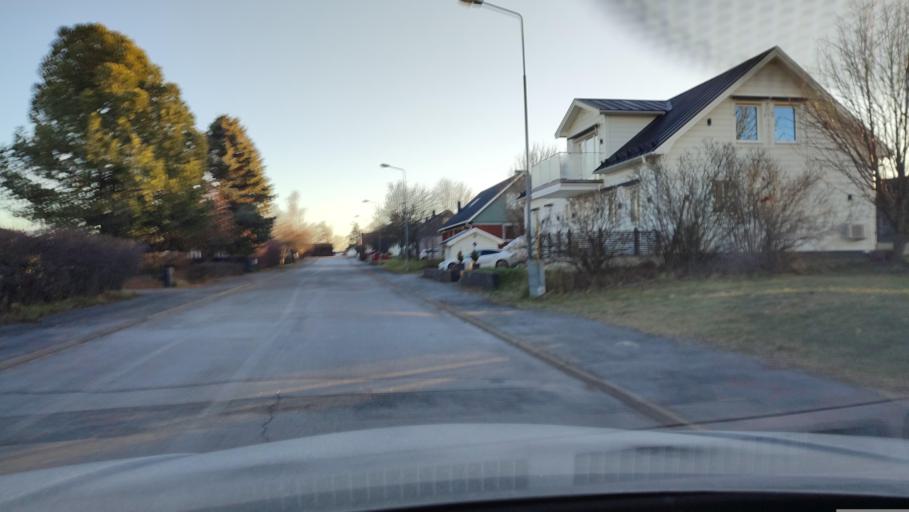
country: SE
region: Vaesterbotten
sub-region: Skelleftea Kommun
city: Viken
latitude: 64.7462
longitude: 20.9159
